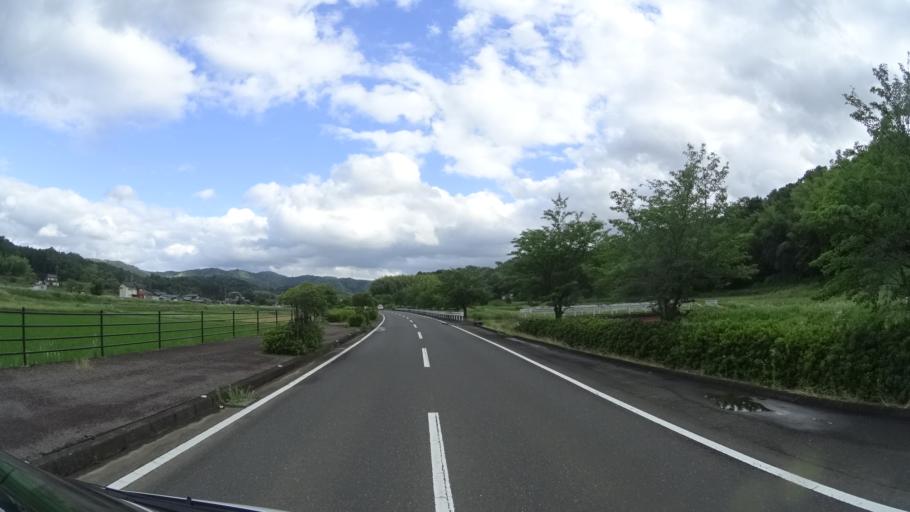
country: JP
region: Kyoto
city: Ayabe
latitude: 35.3424
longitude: 135.2900
